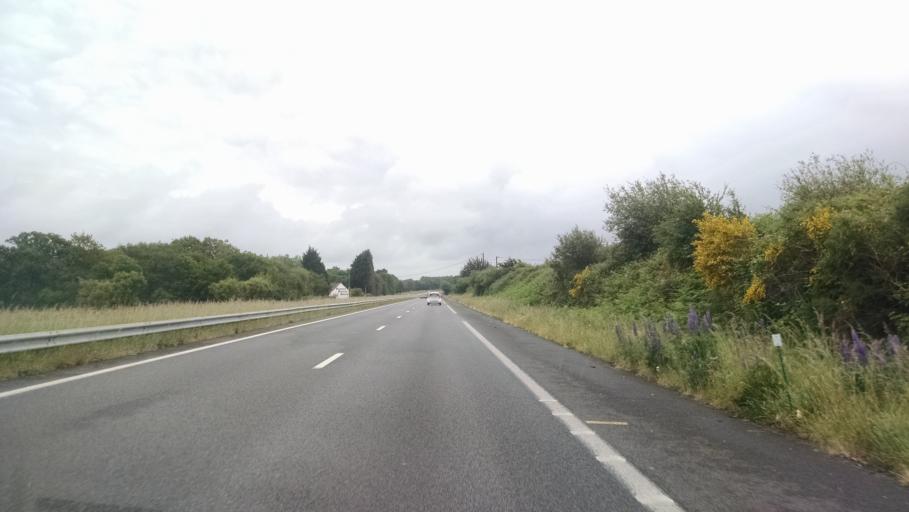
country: FR
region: Brittany
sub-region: Departement du Morbihan
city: Landaul
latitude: 47.7211
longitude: -3.0700
